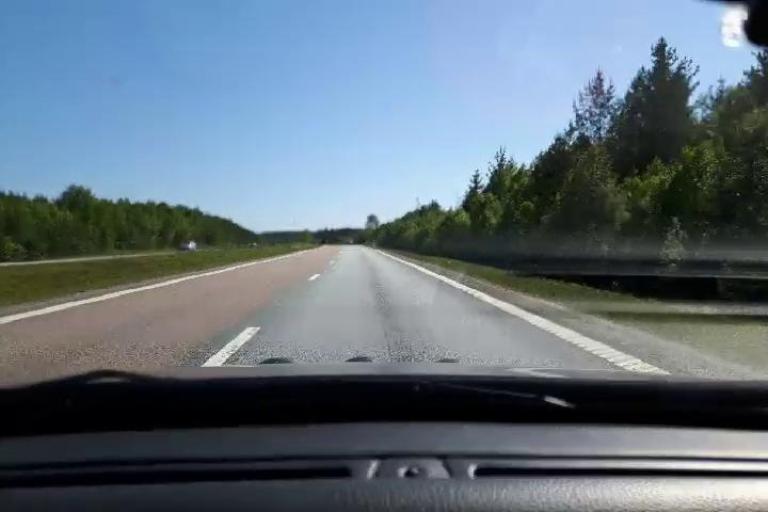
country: SE
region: Gaevleborg
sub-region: Hudiksvalls Kommun
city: Iggesund
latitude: 61.4935
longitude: 16.9839
